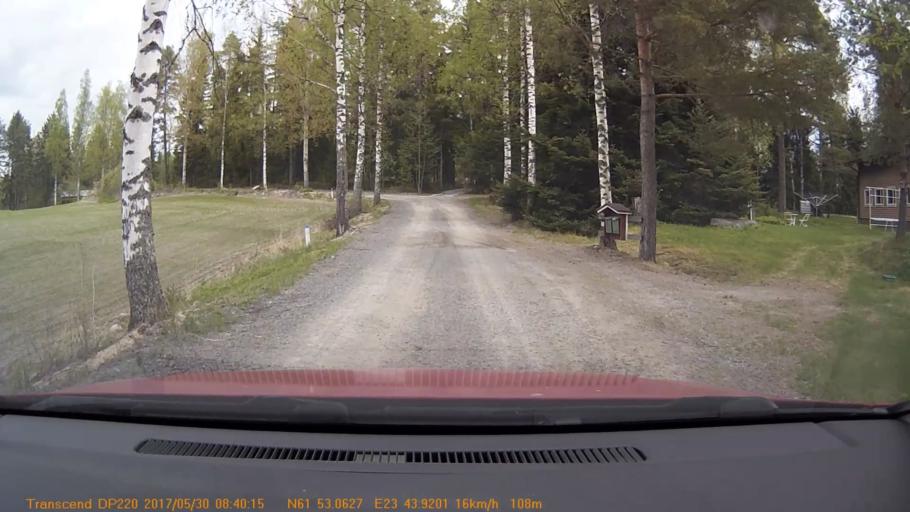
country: FI
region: Pirkanmaa
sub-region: Tampere
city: Kuru
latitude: 61.8845
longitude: 23.7327
